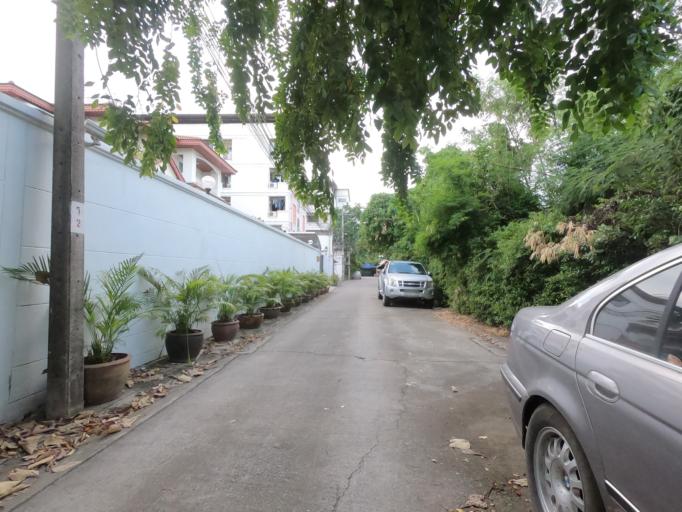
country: TH
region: Bangkok
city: Lat Phrao
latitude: 13.8204
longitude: 100.6125
